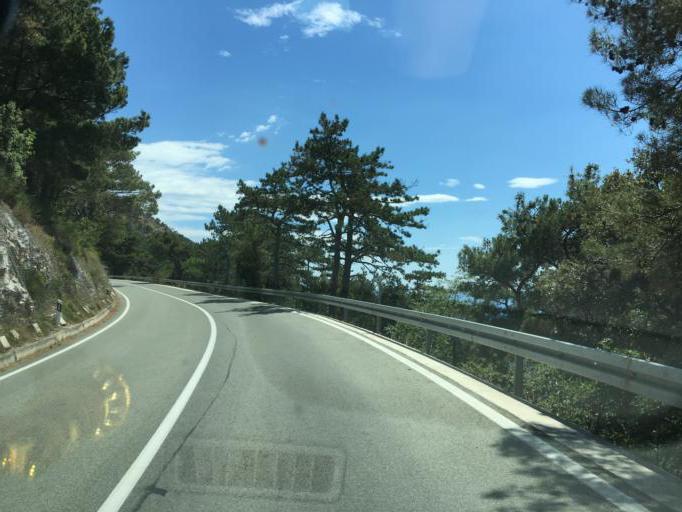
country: HR
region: Istarska
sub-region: Grad Labin
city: Rabac
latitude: 45.1329
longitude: 14.1876
